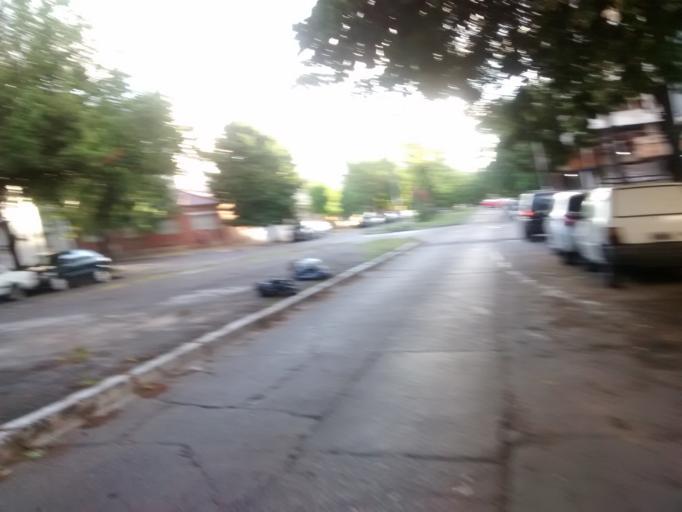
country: AR
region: Buenos Aires
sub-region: Partido de La Plata
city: La Plata
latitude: -34.9100
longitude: -57.9670
